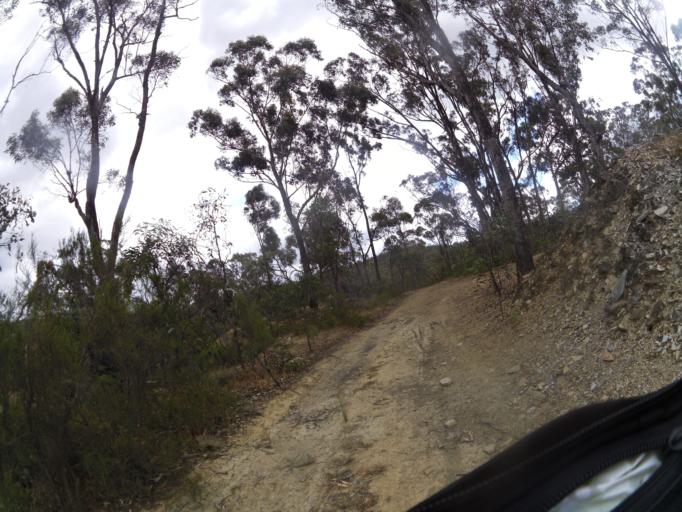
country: AU
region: Victoria
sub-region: Mount Alexander
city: Castlemaine
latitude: -37.0733
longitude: 144.2546
